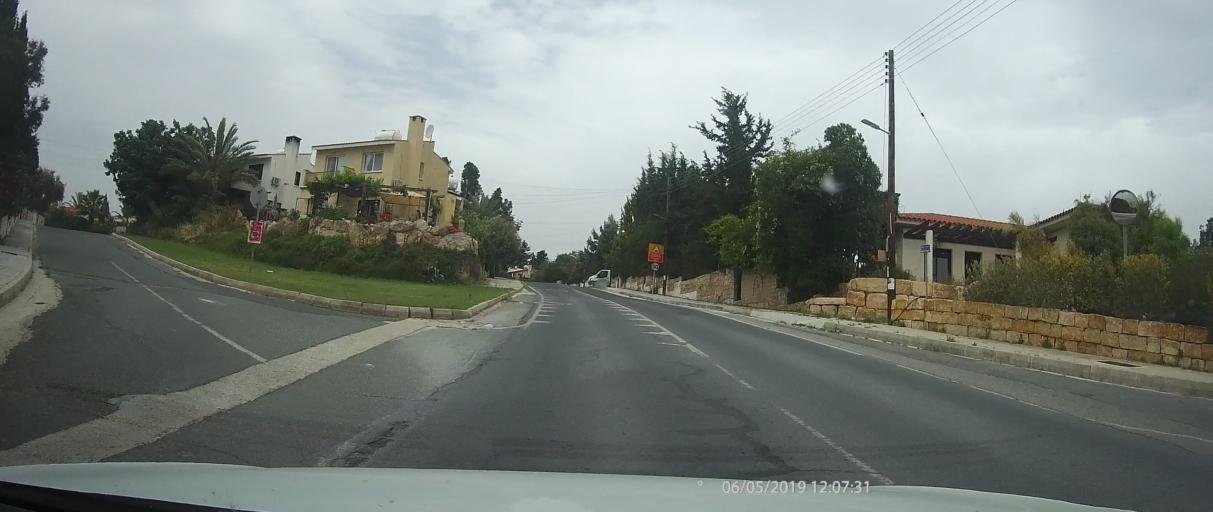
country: CY
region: Pafos
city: Tala
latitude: 34.8281
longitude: 32.4285
